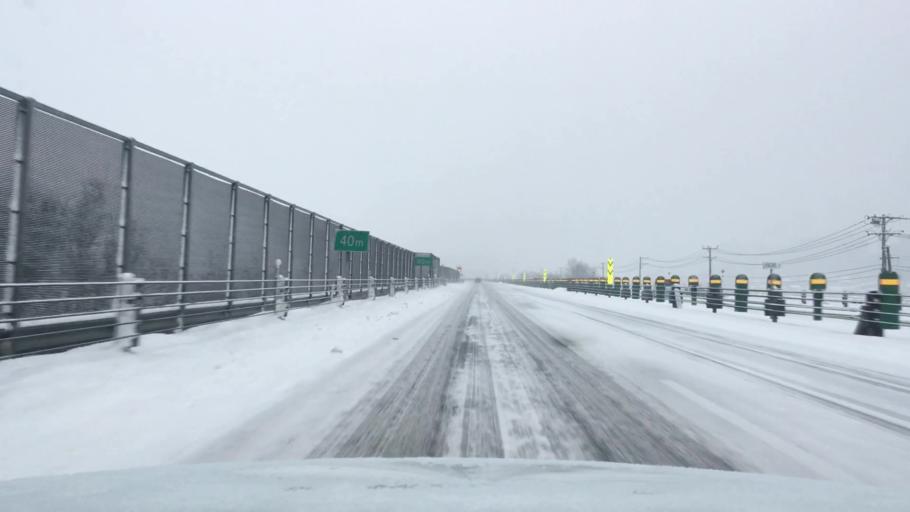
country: JP
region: Akita
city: Hanawa
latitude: 40.2853
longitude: 140.7597
